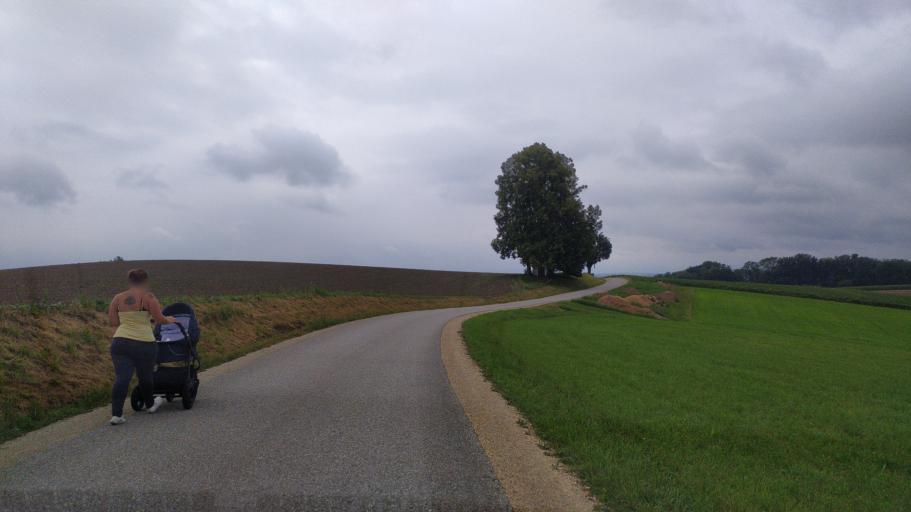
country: AT
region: Upper Austria
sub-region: Politischer Bezirk Perg
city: Perg
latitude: 48.2407
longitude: 14.6778
